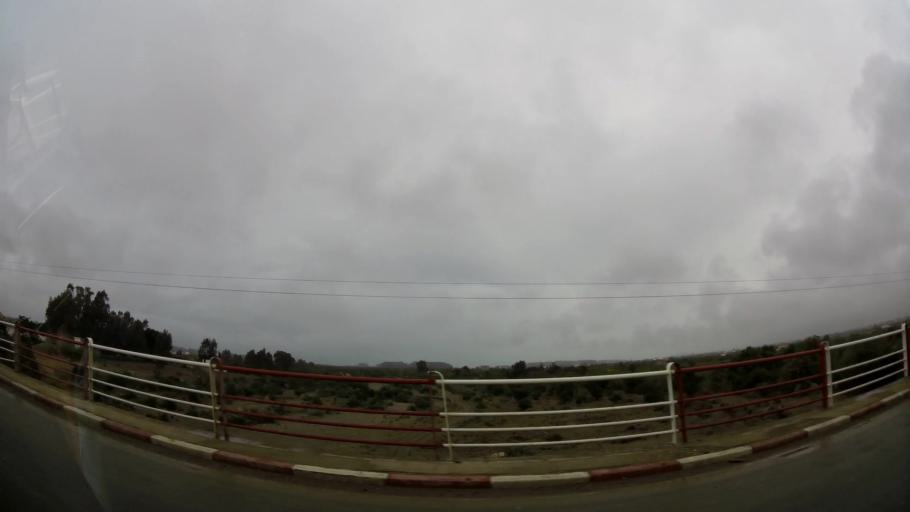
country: MA
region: Taza-Al Hoceima-Taounate
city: Imzourene
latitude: 35.1828
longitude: -3.8809
